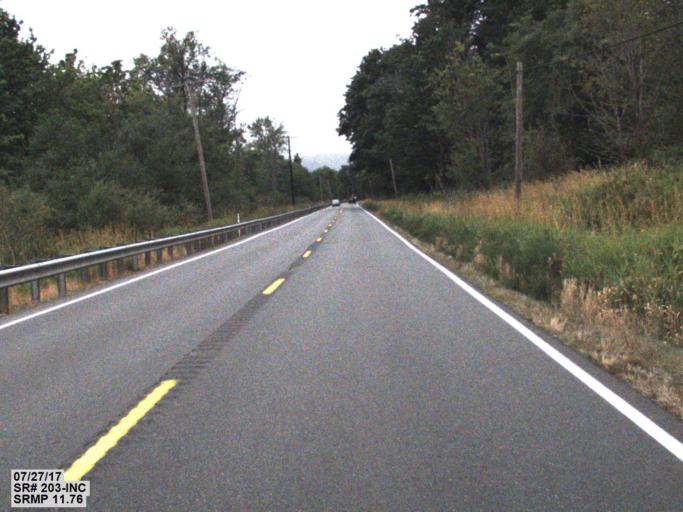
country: US
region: Washington
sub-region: King County
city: Duvall
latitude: 47.6981
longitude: -121.9771
